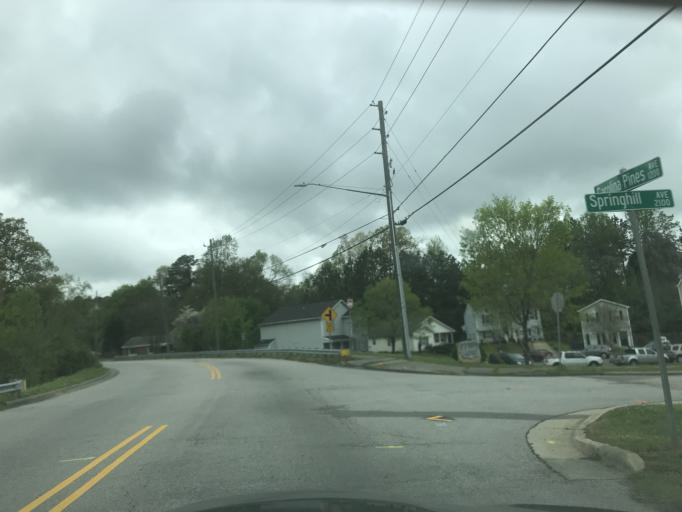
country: US
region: North Carolina
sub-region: Wake County
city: Raleigh
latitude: 35.7507
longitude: -78.6593
